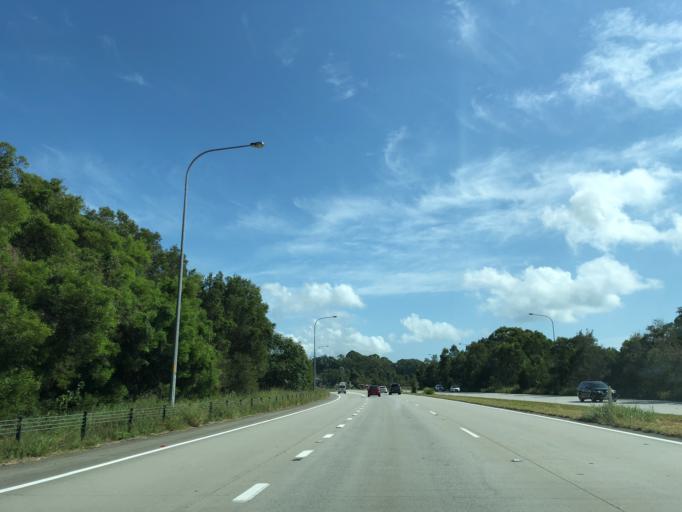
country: AU
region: New South Wales
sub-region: Byron Shire
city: Brunswick Heads
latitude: -28.5629
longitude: 153.5423
